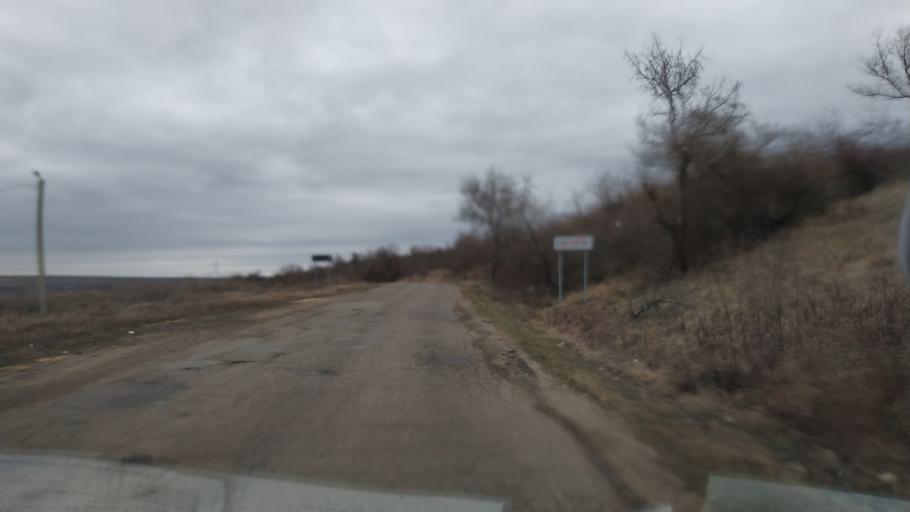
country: MD
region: Causeni
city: Causeni
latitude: 46.6644
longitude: 29.4524
